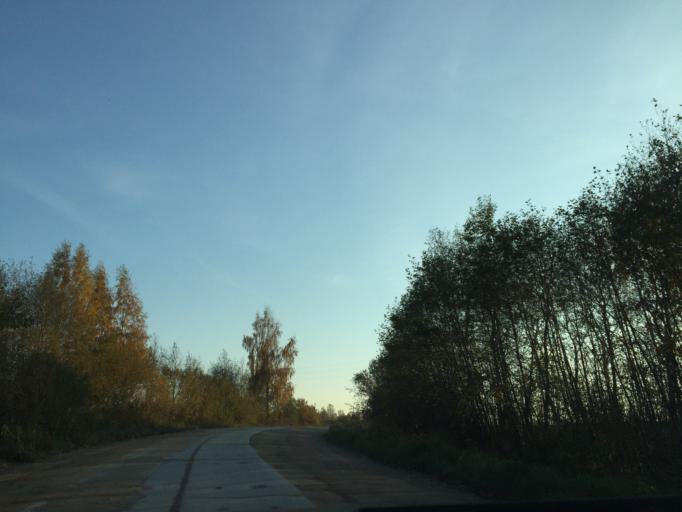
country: LV
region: Vainode
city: Vainode
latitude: 56.5526
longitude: 21.8429
